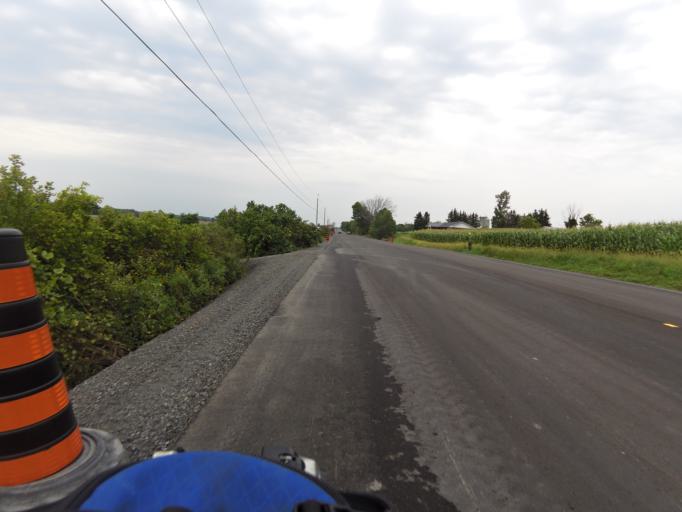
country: CA
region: Ontario
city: Ottawa
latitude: 45.1761
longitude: -75.4414
